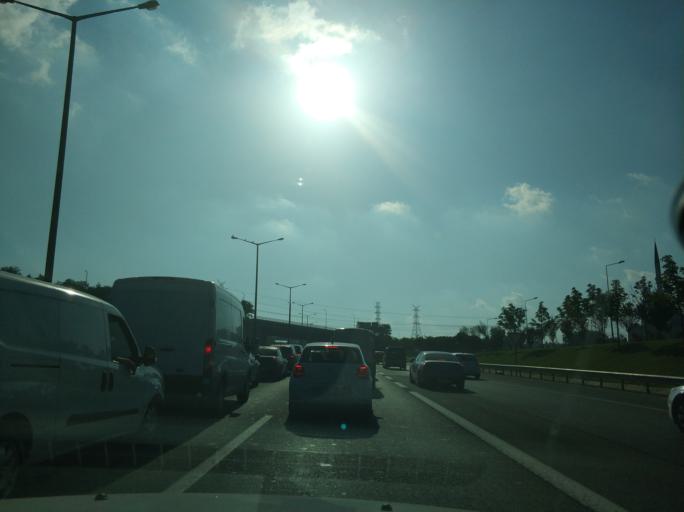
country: TR
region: Istanbul
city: Sisli
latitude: 41.0999
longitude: 28.9654
